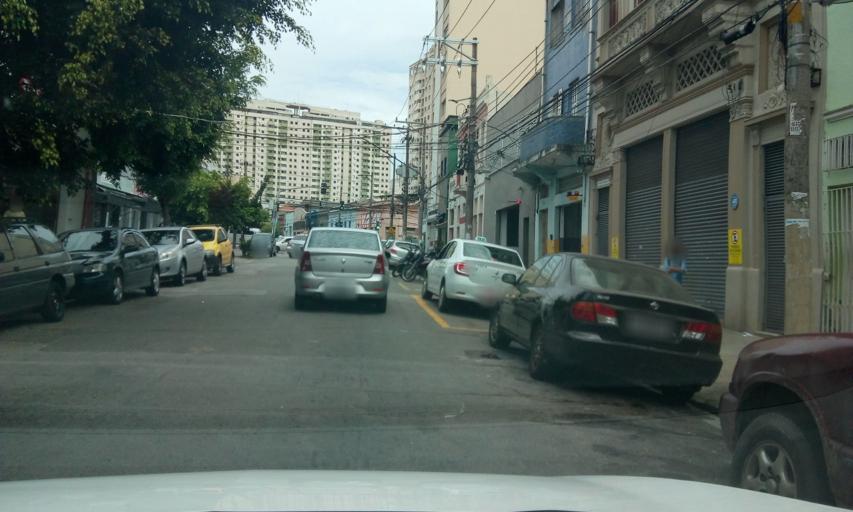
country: BR
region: Sao Paulo
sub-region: Sao Paulo
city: Sao Paulo
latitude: -23.5304
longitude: -46.6541
